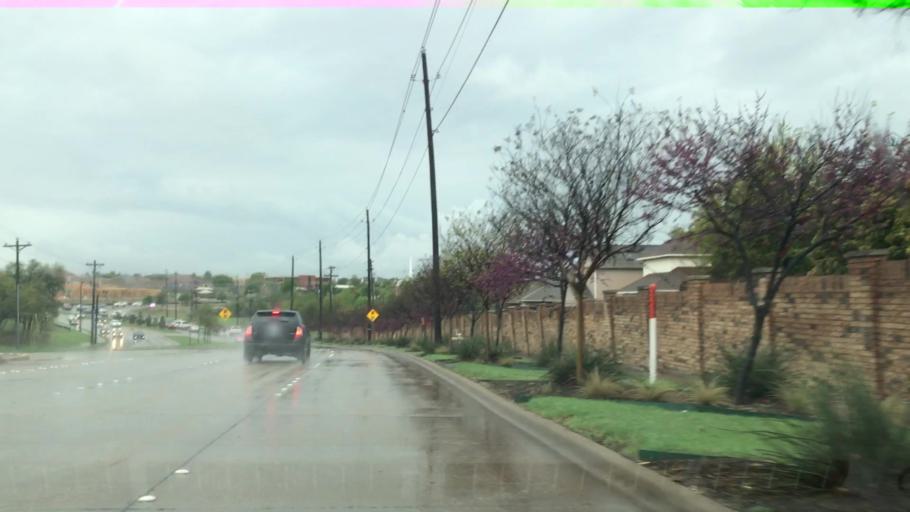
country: US
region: Texas
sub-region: Denton County
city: The Colony
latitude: 33.0384
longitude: -96.8834
